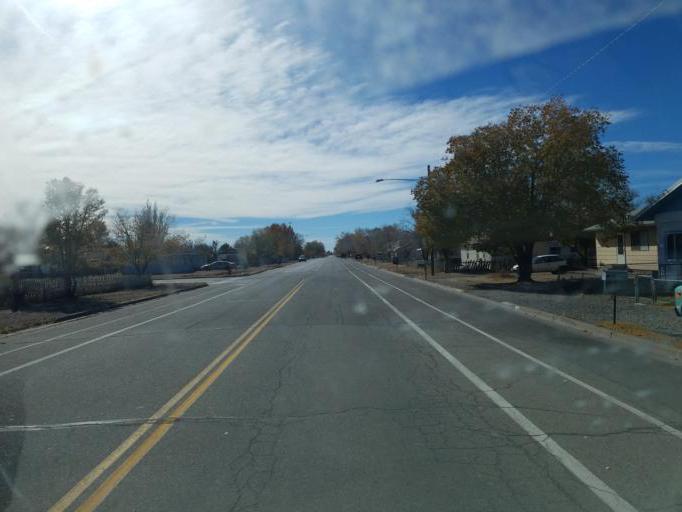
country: US
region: Colorado
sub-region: Alamosa County
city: Alamosa
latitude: 37.4607
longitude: -105.8702
